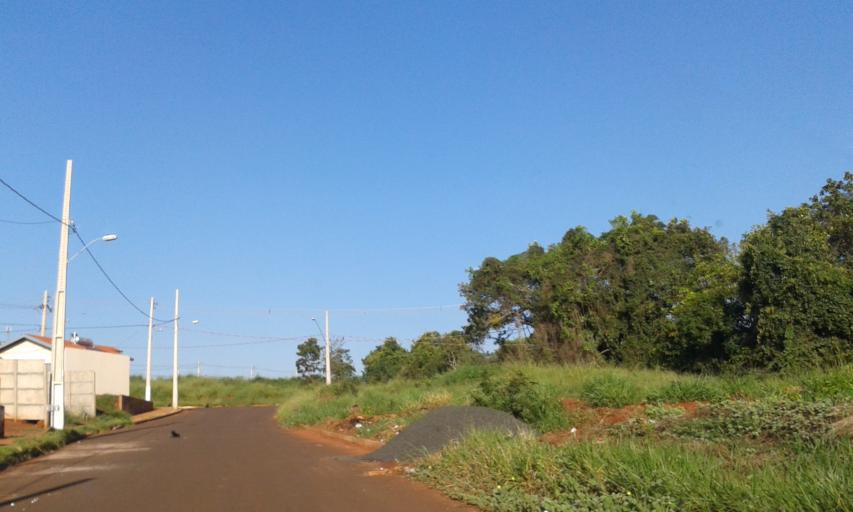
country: BR
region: Minas Gerais
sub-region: Ituiutaba
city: Ituiutaba
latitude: -19.0136
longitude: -49.4509
